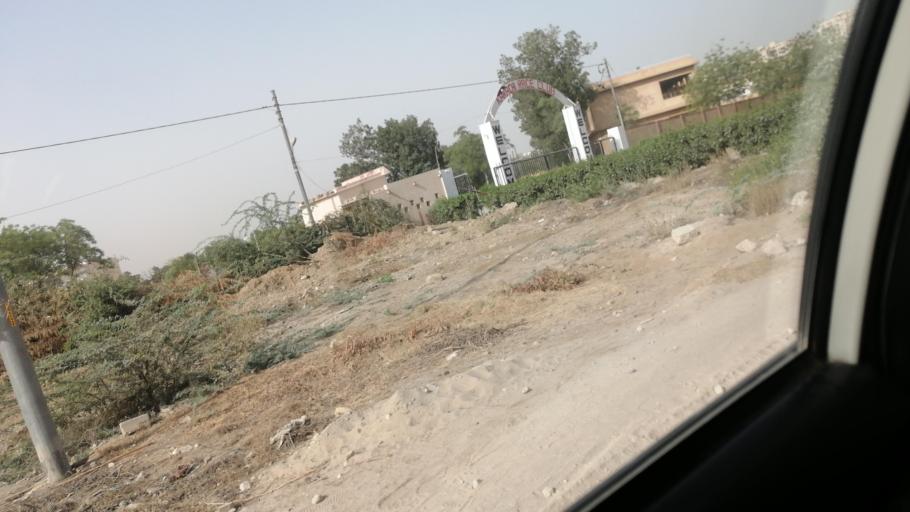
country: PK
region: Sindh
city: Malir Cantonment
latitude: 24.9380
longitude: 67.1641
